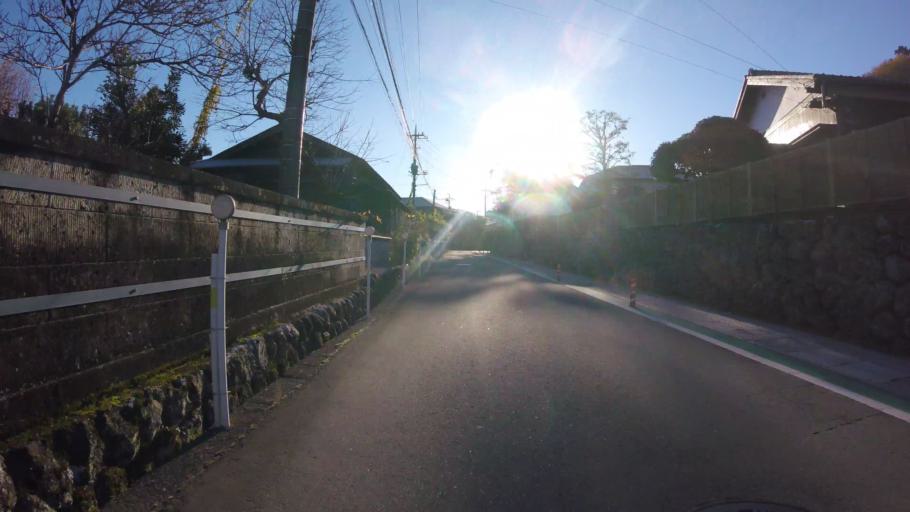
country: JP
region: Shizuoka
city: Mishima
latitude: 34.9869
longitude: 138.9483
